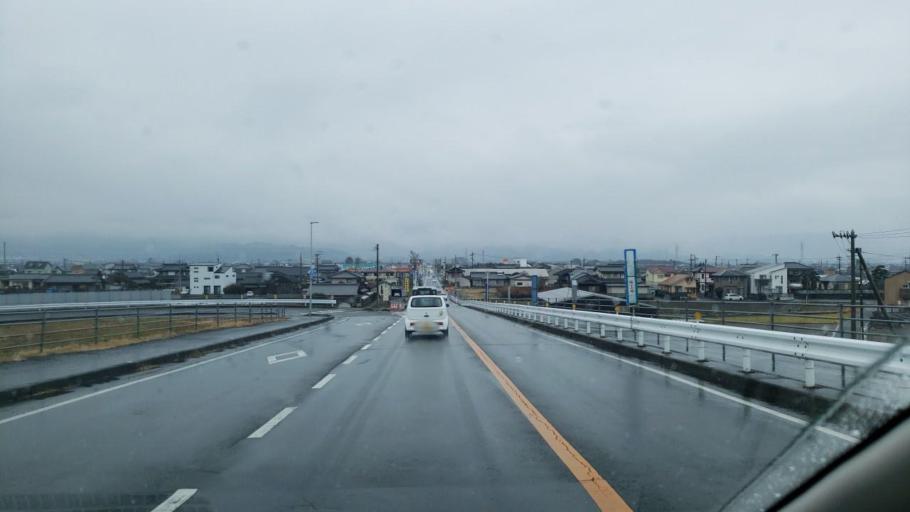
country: JP
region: Tokushima
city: Ishii
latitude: 34.1087
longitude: 134.4368
